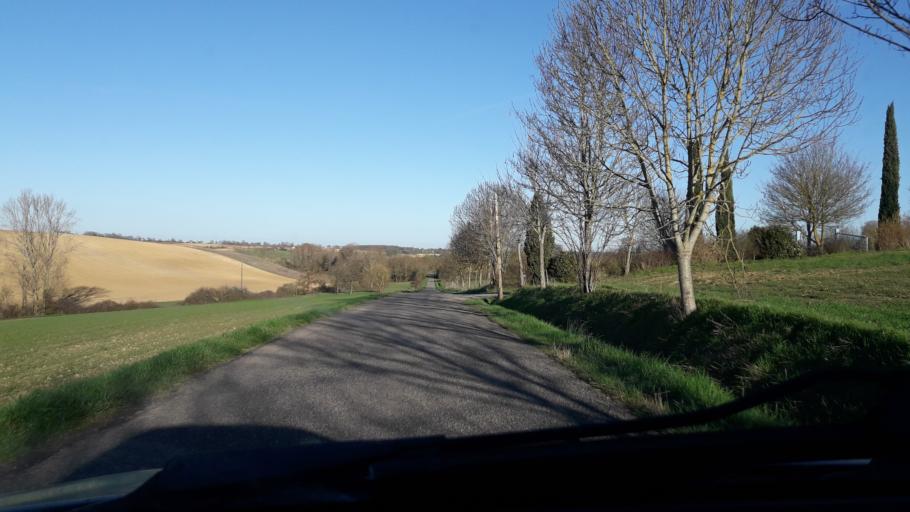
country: FR
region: Midi-Pyrenees
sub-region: Departement du Gers
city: Gimont
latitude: 43.6255
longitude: 0.9850
